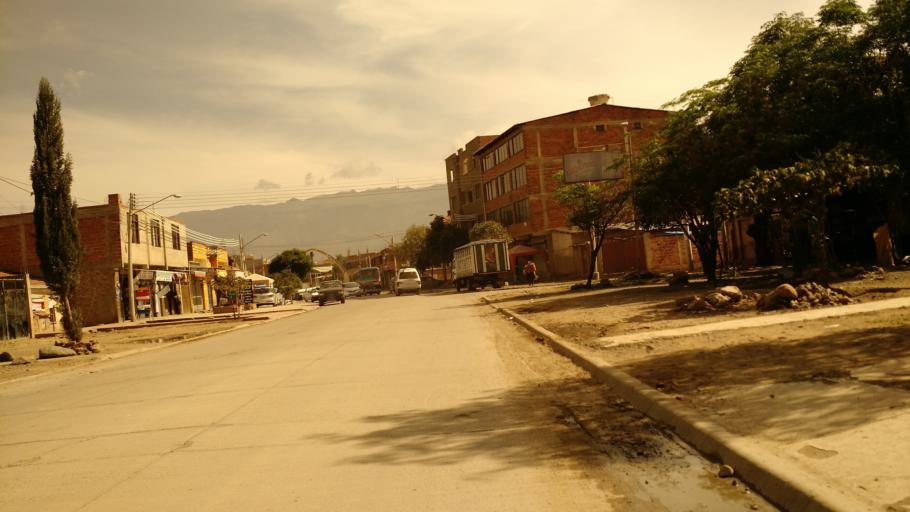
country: BO
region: Cochabamba
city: Cochabamba
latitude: -17.4307
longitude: -66.1589
